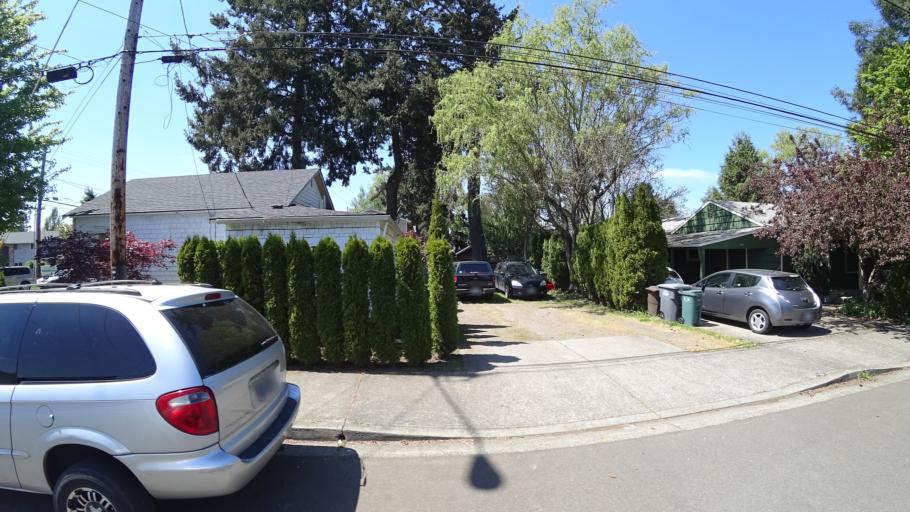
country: US
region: Oregon
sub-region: Washington County
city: Hillsboro
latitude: 45.5176
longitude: -122.9665
